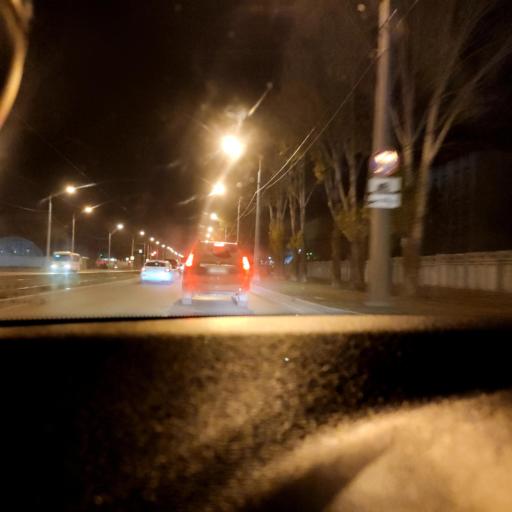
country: RU
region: Samara
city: Samara
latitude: 53.2000
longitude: 50.2586
